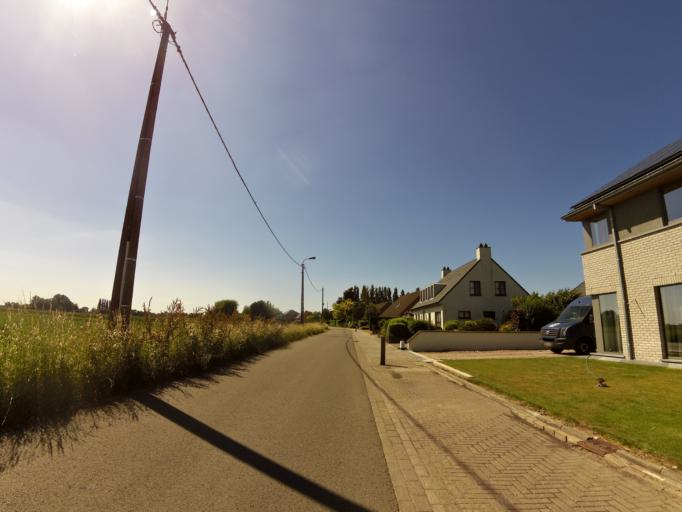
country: BE
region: Flanders
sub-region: Provincie West-Vlaanderen
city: Oudenburg
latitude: 51.1817
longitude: 2.9929
